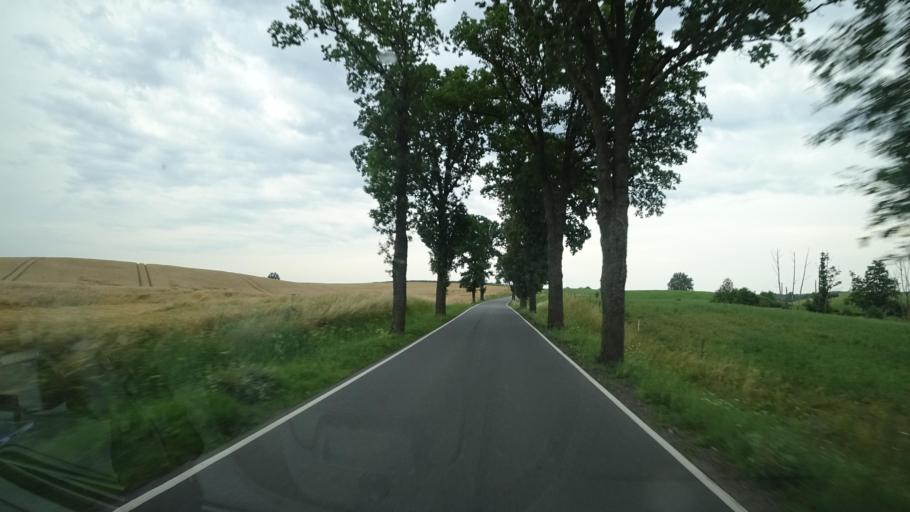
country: PL
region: Warmian-Masurian Voivodeship
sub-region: Powiat mragowski
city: Mikolajki
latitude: 53.8666
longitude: 21.7274
